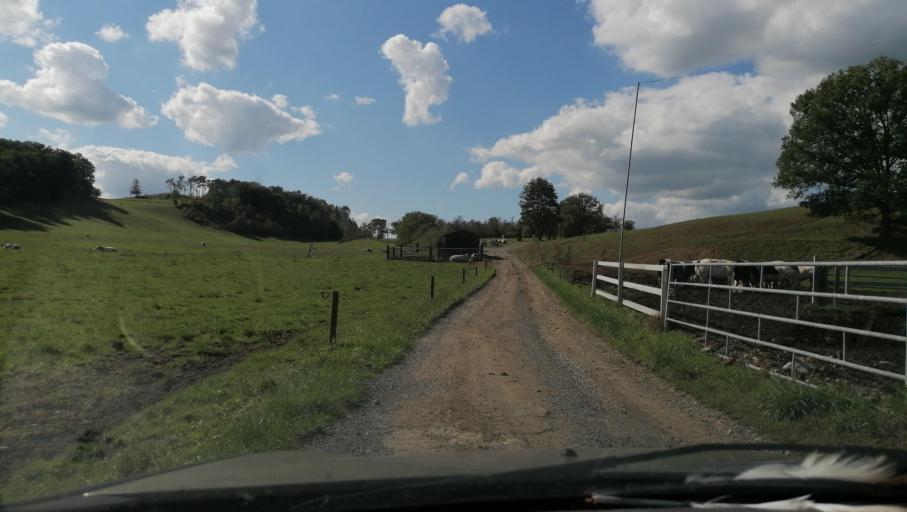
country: BE
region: Wallonia
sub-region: Province de Namur
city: Rochefort
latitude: 50.1250
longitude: 5.1682
